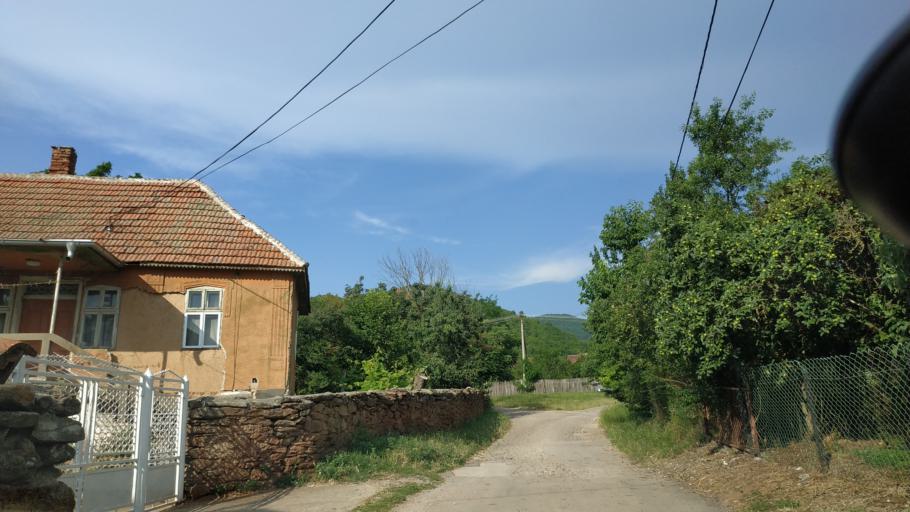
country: RS
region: Central Serbia
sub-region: Nisavski Okrug
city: Aleksinac
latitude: 43.6046
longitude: 21.6928
